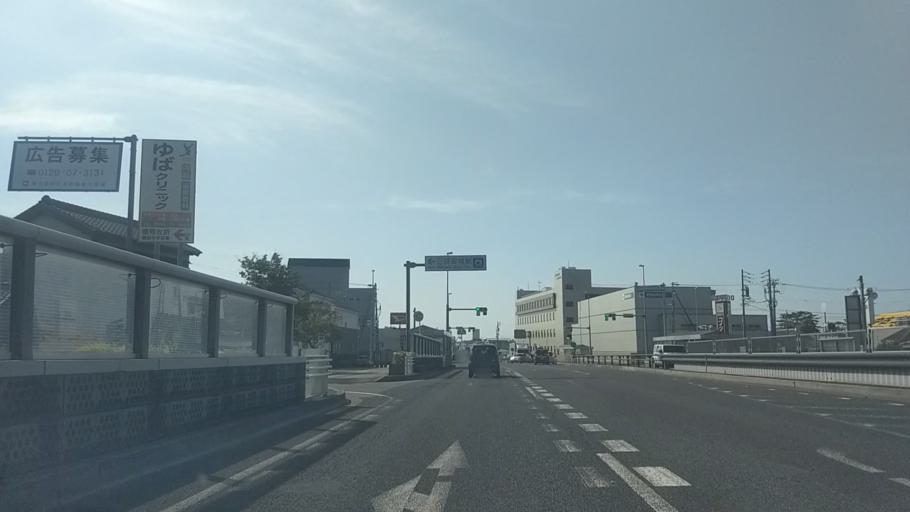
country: JP
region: Aichi
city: Anjo
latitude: 34.9920
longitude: 137.0798
